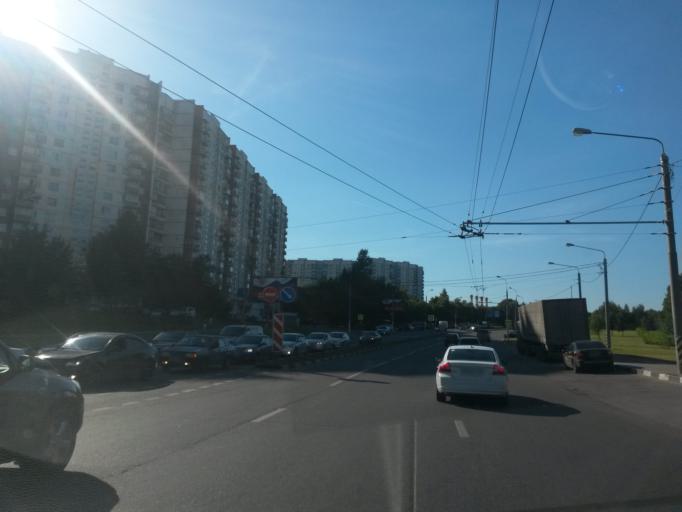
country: RU
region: Moscow
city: Yasenevo
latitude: 55.6080
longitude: 37.5248
